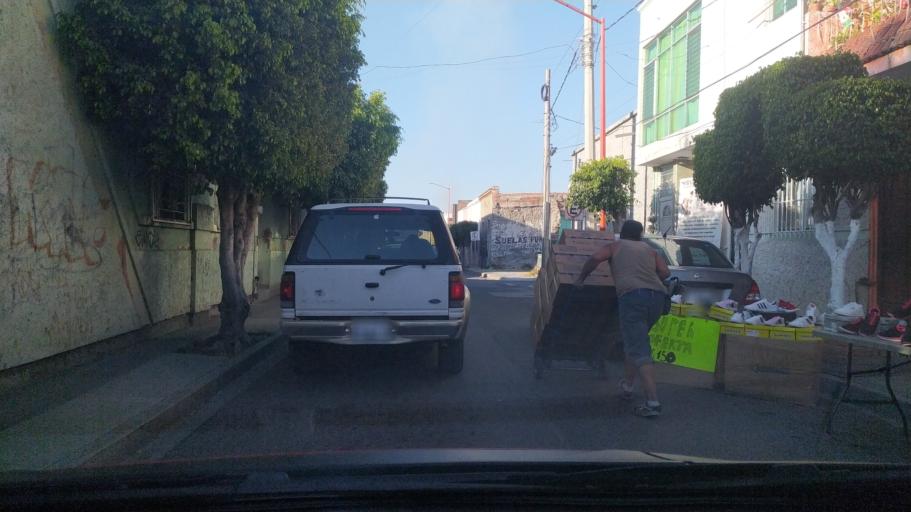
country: MX
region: Guanajuato
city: San Francisco del Rincon
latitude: 21.0171
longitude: -101.8553
